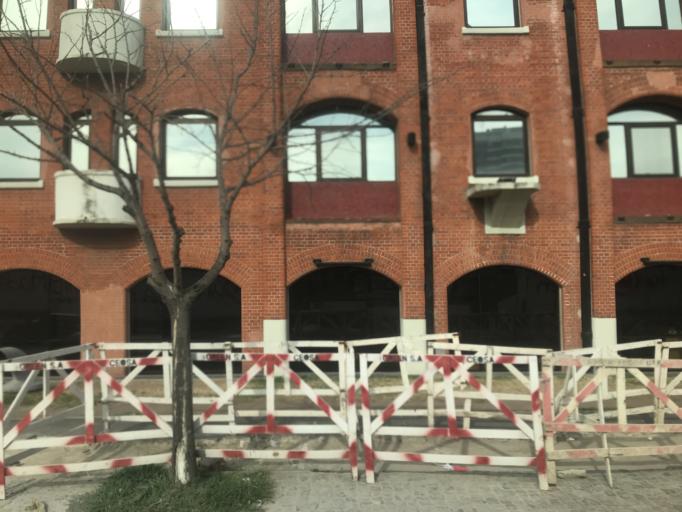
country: AR
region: Buenos Aires F.D.
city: Buenos Aires
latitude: -34.6132
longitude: -58.3662
